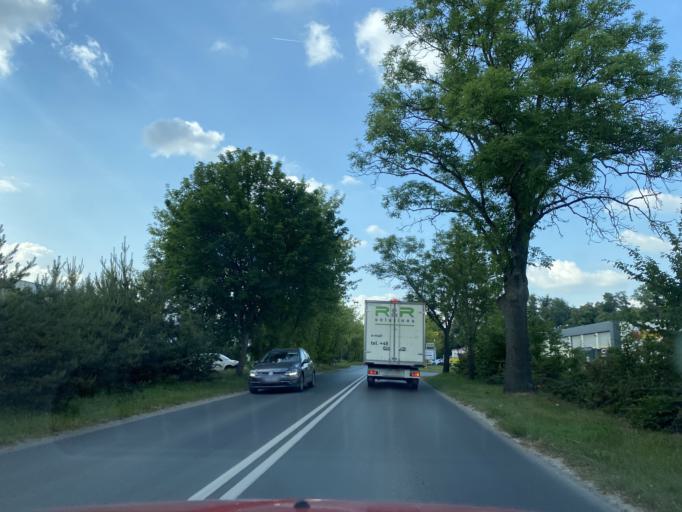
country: PL
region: Greater Poland Voivodeship
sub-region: Powiat poznanski
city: Plewiska
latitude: 52.3803
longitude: 16.7448
